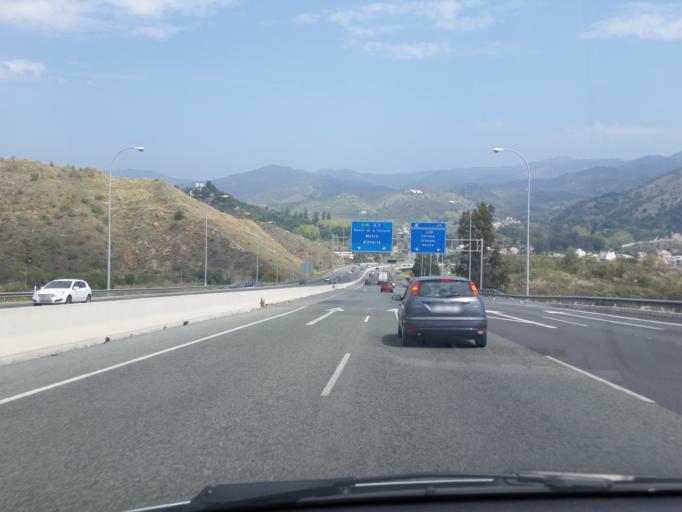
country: ES
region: Andalusia
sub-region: Provincia de Malaga
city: Malaga
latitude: 36.7510
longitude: -4.4315
